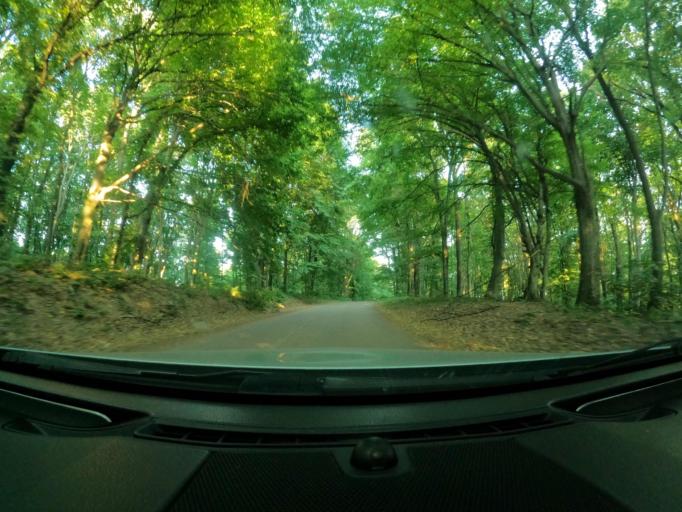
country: RS
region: Autonomna Pokrajina Vojvodina
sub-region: Juznobacki Okrug
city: Beocin
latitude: 45.1549
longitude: 19.7242
